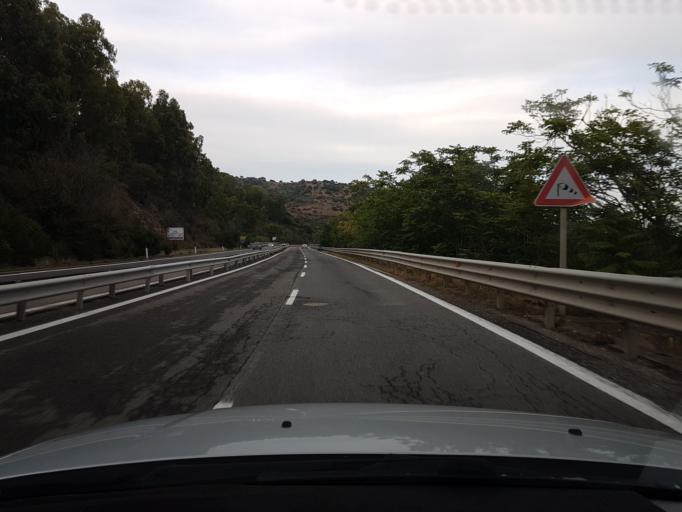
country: IT
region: Sardinia
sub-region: Provincia di Nuoro
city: Nuoro
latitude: 40.3357
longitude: 9.2993
